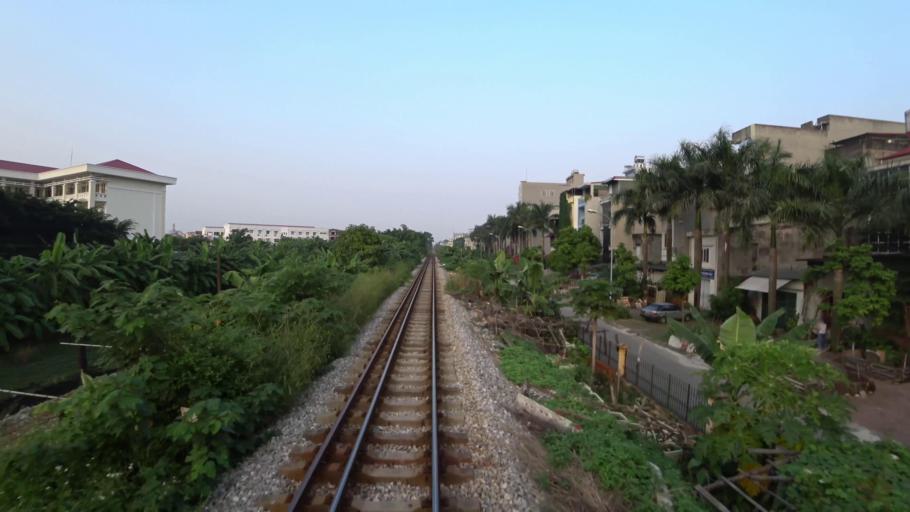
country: VN
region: Ha Noi
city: Trau Quy
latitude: 21.0773
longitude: 105.9082
